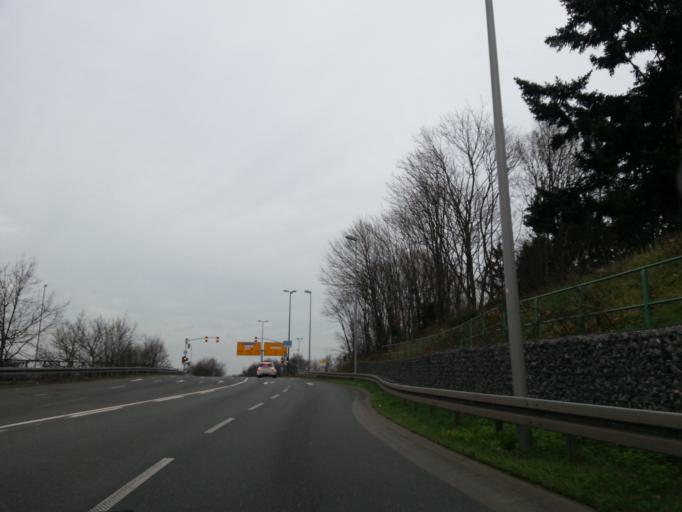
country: DE
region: North Rhine-Westphalia
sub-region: Regierungsbezirk Dusseldorf
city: Dusseldorf
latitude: 51.2703
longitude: 6.7516
